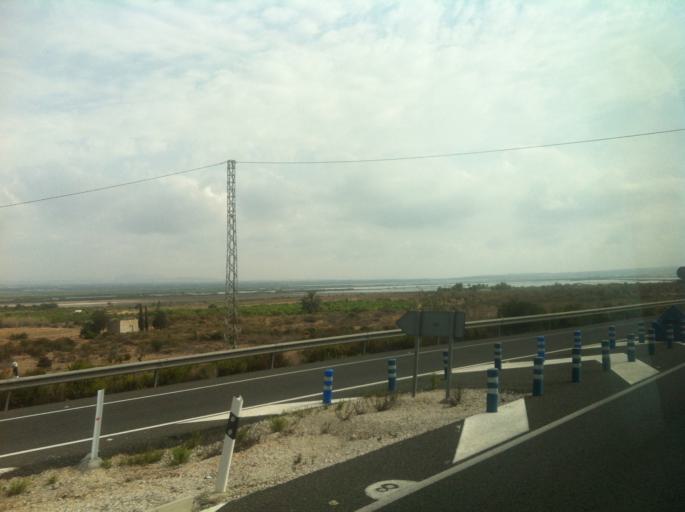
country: ES
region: Valencia
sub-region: Provincia de Alicante
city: Guardamar del Segura
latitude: 38.1594
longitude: -0.6495
